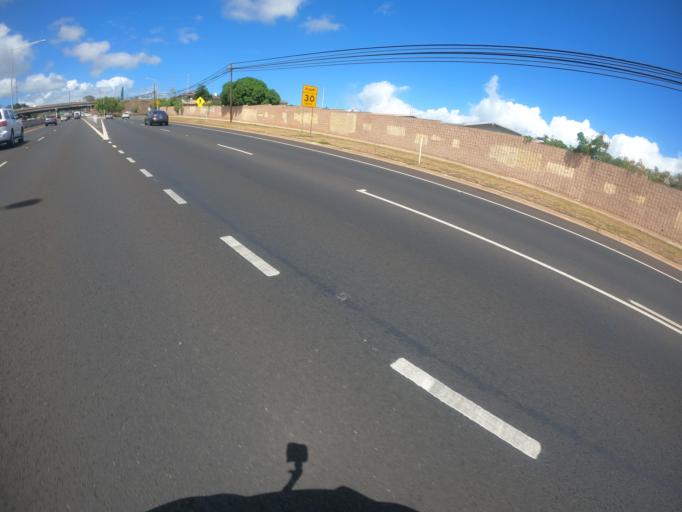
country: US
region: Hawaii
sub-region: Honolulu County
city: Royal Kunia
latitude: 21.3823
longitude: -158.0308
